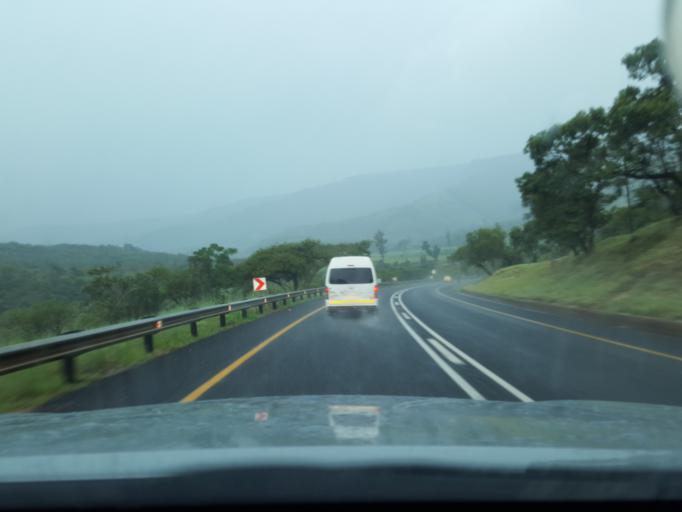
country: ZA
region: Mpumalanga
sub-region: Ehlanzeni District
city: Nelspruit
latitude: -25.5470
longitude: 30.6837
